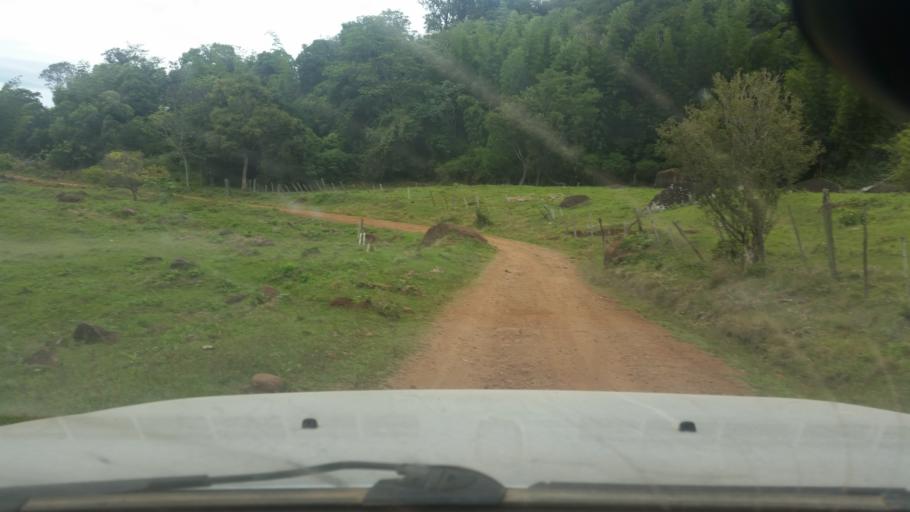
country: PY
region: Guaira
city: Independencia
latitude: -25.8117
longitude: -56.2753
